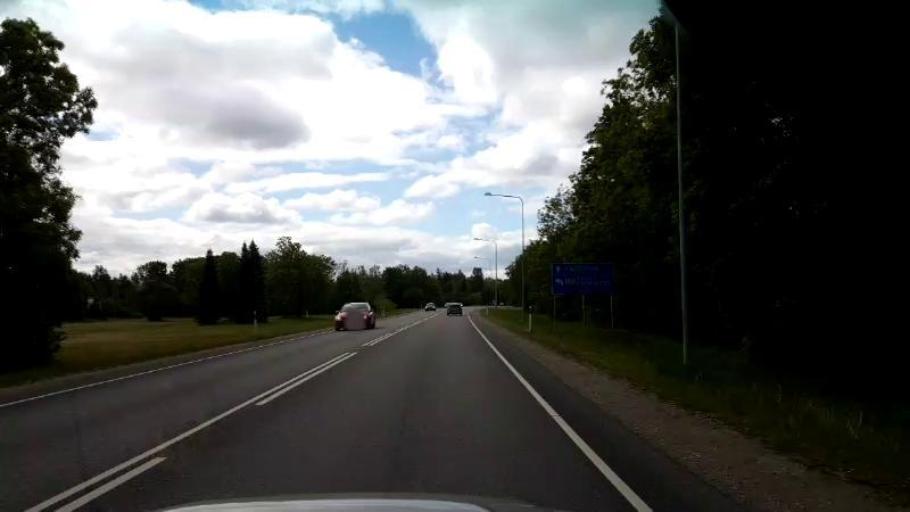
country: EE
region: Paernumaa
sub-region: Halinga vald
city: Parnu-Jaagupi
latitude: 58.6138
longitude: 24.5128
